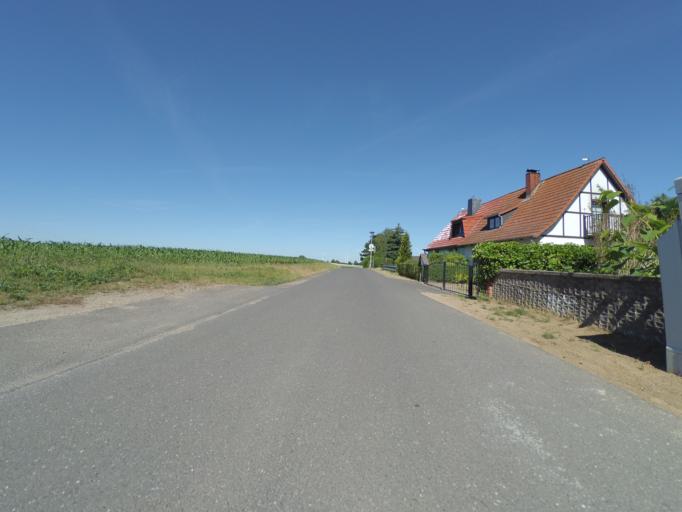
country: DE
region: Mecklenburg-Vorpommern
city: Plau am See
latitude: 53.4893
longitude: 12.2762
